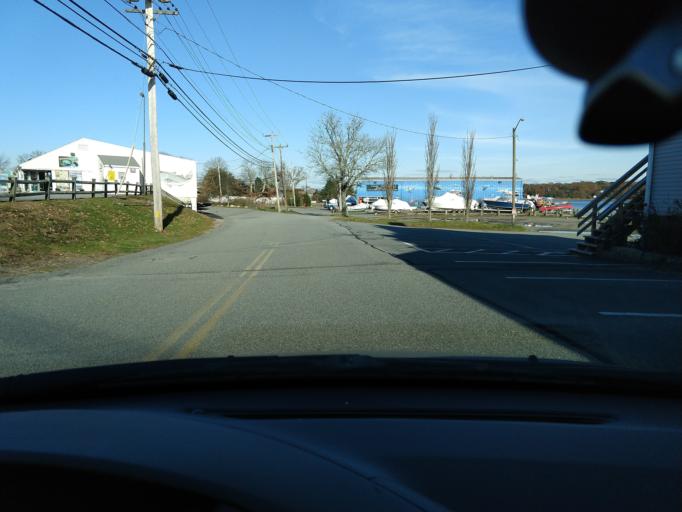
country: US
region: Massachusetts
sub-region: Barnstable County
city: Orleans
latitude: 41.7948
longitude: -69.9830
